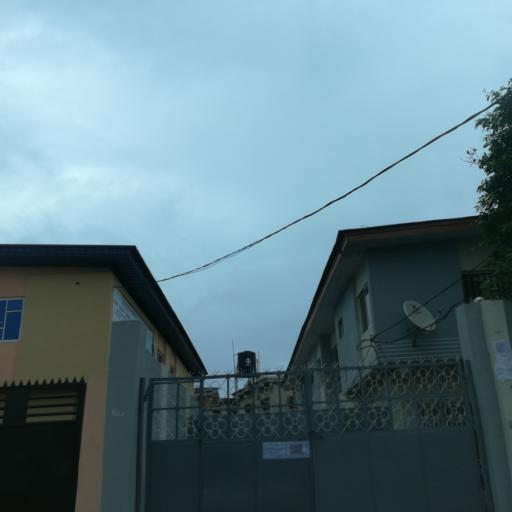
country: NG
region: Lagos
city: Oshodi
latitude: 6.5538
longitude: 3.3428
